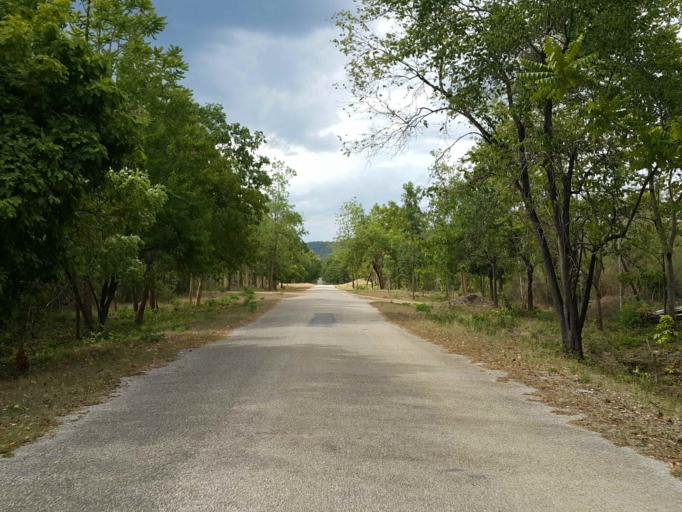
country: TH
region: Sukhothai
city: Thung Saliam
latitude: 17.3365
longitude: 99.4239
